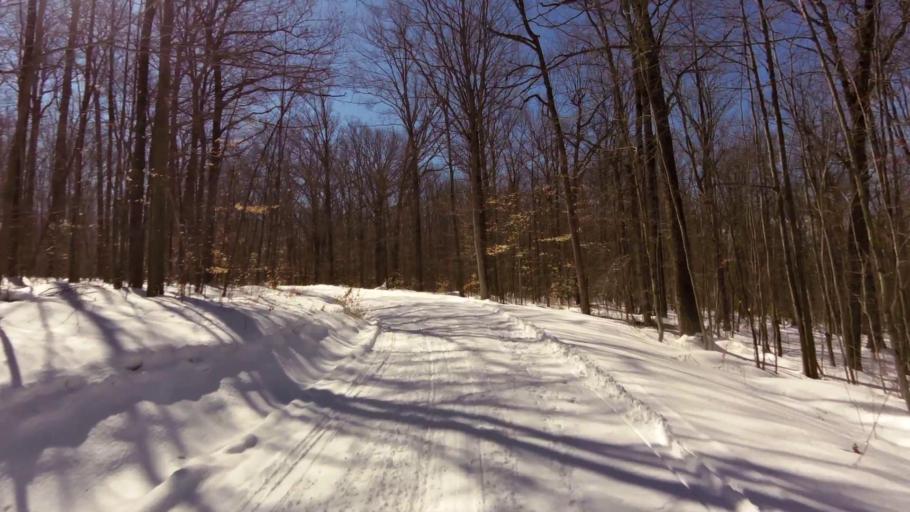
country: US
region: New York
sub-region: Allegany County
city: Houghton
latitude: 42.3540
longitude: -78.1950
